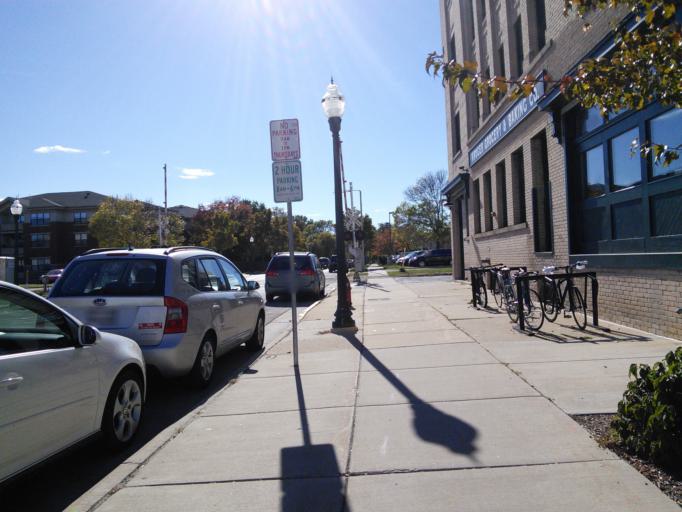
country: US
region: Wisconsin
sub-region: Dane County
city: Madison
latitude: 43.0674
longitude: -89.3923
